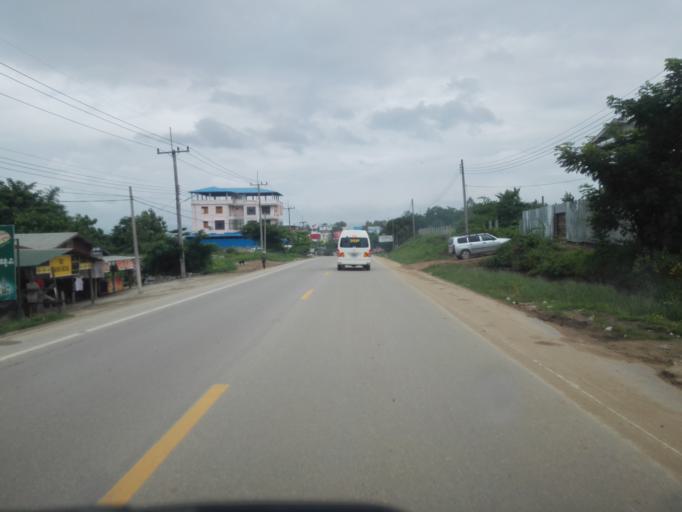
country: TH
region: Tak
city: Mae Sot
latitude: 16.6861
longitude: 98.4916
